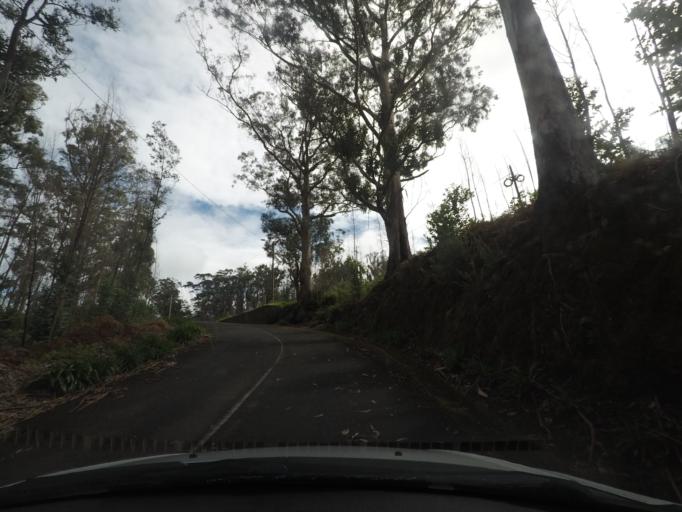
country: PT
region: Madeira
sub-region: Calheta
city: Faja da Ovelha
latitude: 32.8290
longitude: -17.2255
